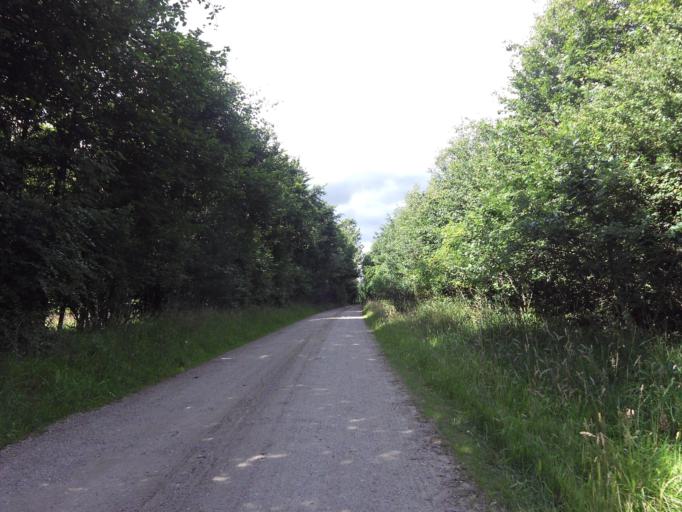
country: DK
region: South Denmark
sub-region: Haderslev Kommune
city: Vojens
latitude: 55.3199
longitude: 9.1978
